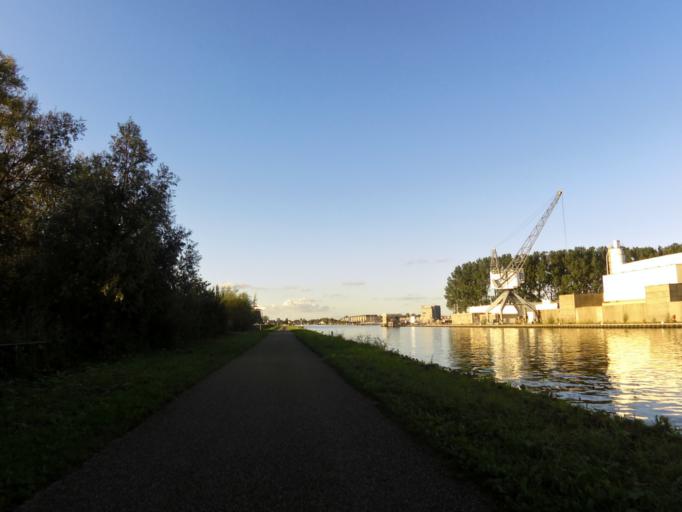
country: NL
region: South Holland
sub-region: Gemeente Alphen aan den Rijn
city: Alphen aan den Rijn
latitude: 52.1509
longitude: 4.6448
